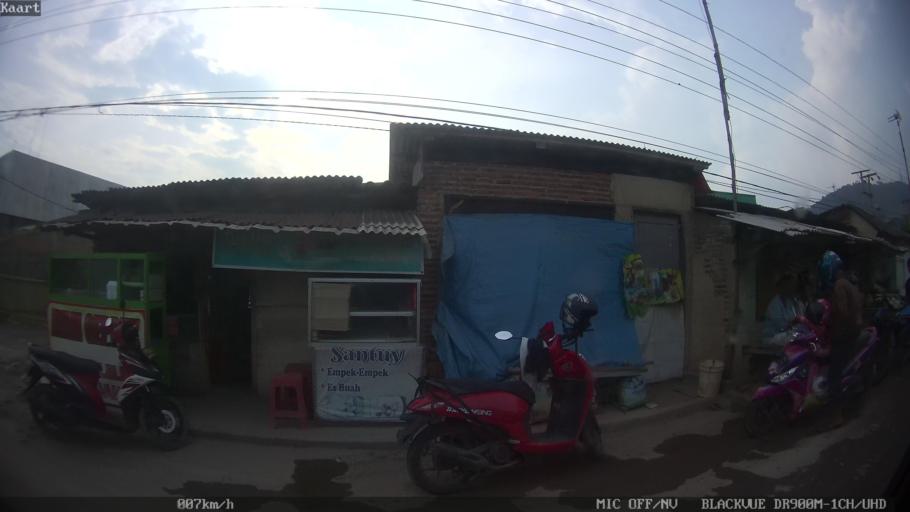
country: ID
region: Lampung
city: Panjang
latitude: -5.4484
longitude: 105.3097
